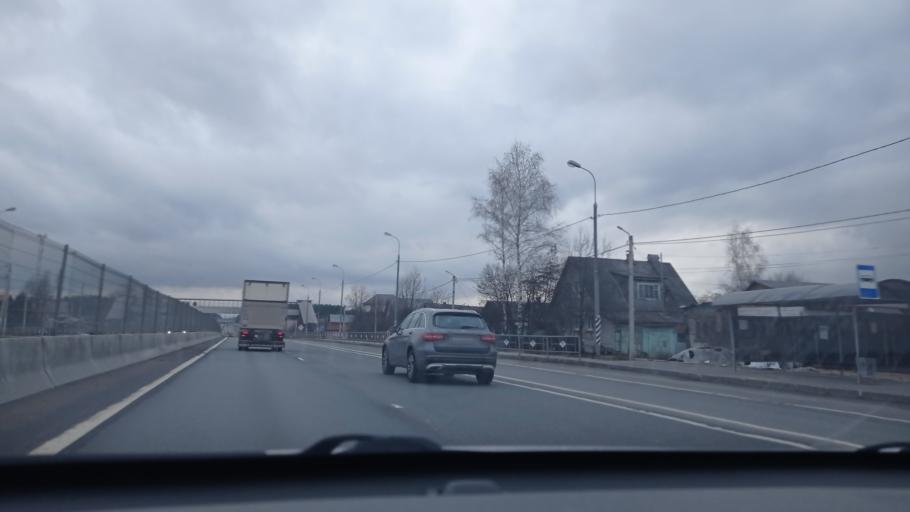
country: RU
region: Vladimir
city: Pokrov
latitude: 55.9165
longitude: 39.1634
